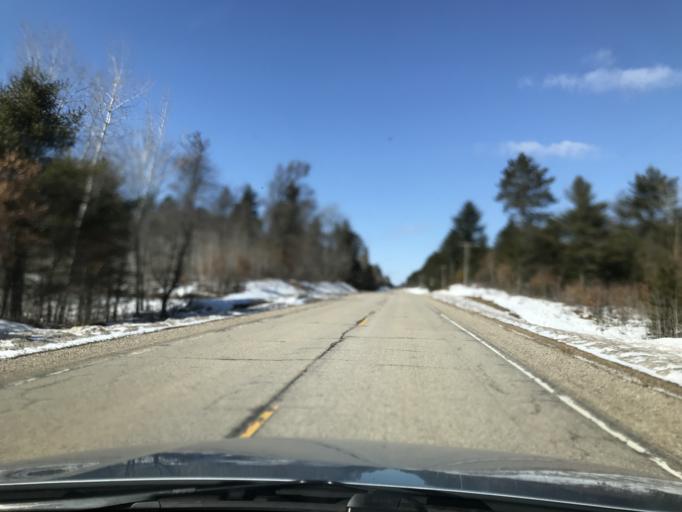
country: US
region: Wisconsin
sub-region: Marinette County
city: Niagara
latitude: 45.3868
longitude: -88.0997
